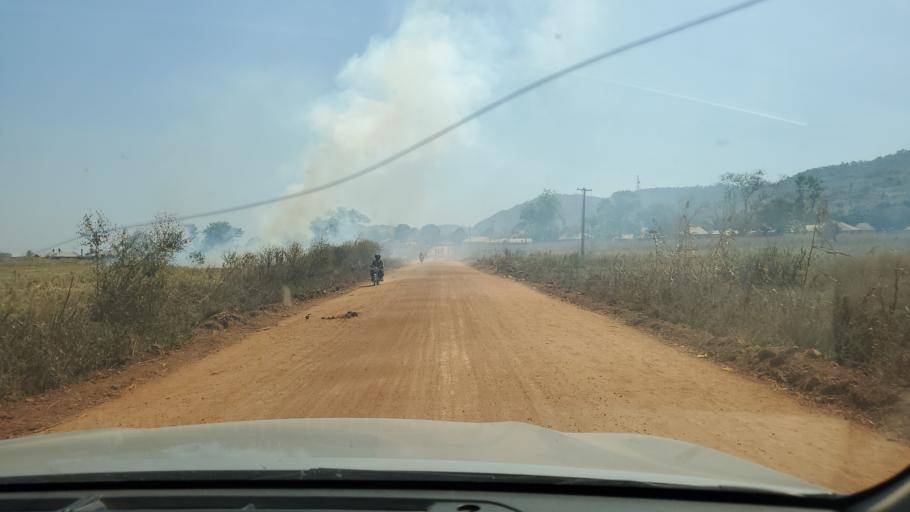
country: NG
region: Niger
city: Gawu Babangida
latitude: 9.2171
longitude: 6.8422
